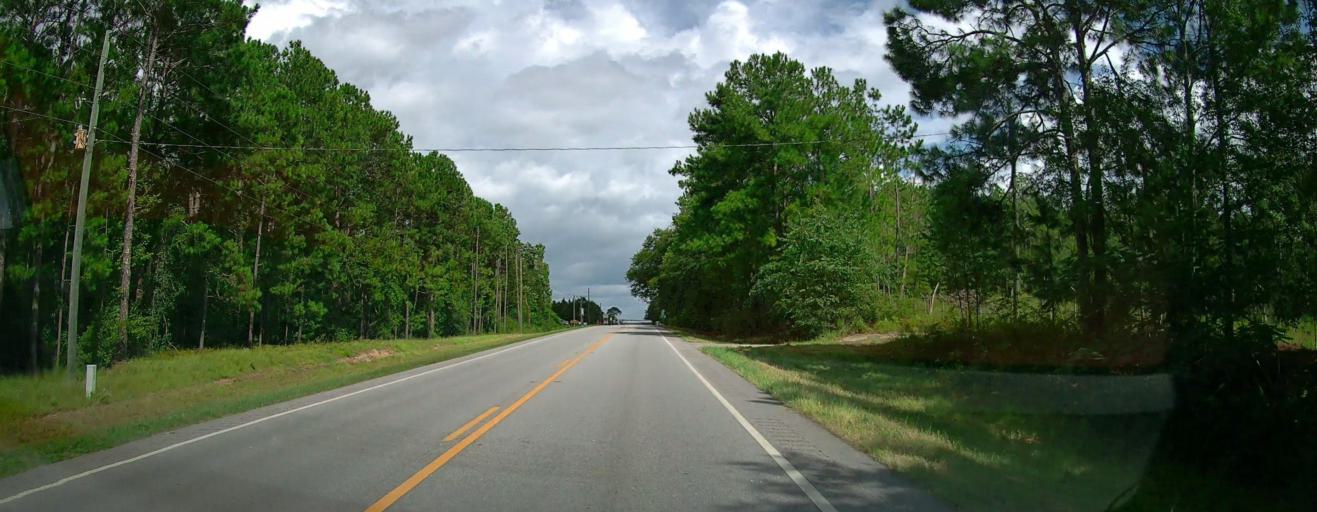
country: US
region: Georgia
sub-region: Coffee County
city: Broxton
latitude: 31.5728
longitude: -83.0320
